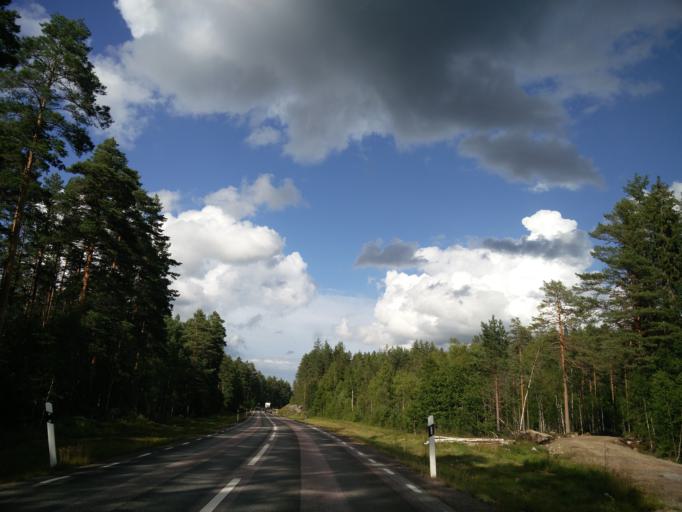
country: SE
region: Vaermland
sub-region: Torsby Kommun
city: Torsby
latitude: 60.3246
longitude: 13.1240
